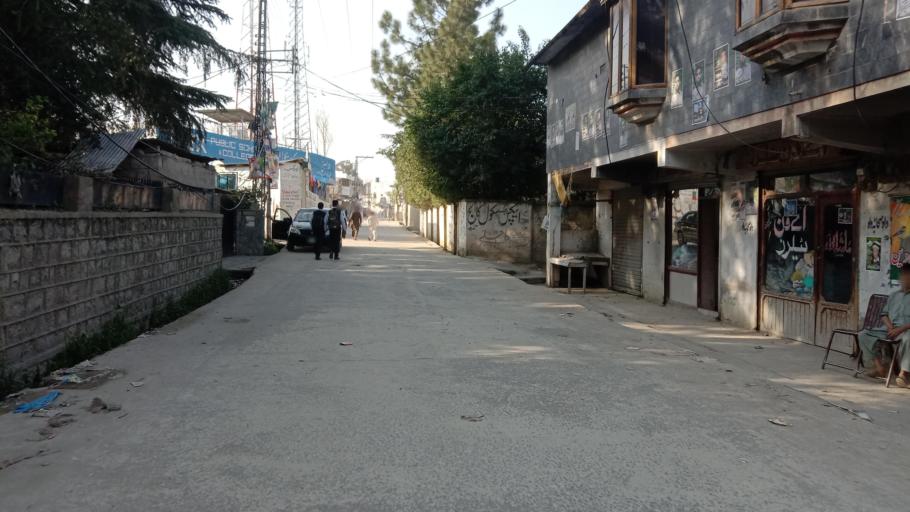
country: PK
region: Khyber Pakhtunkhwa
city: Abbottabad
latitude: 34.1995
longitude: 73.2277
